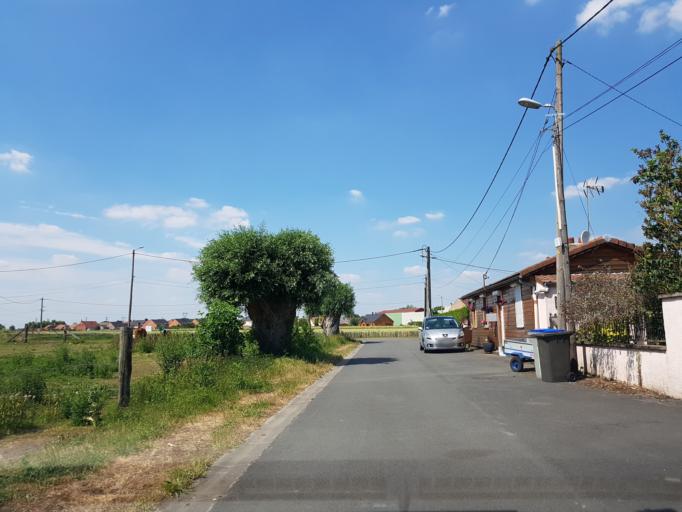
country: FR
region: Nord-Pas-de-Calais
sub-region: Departement du Nord
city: Roeulx
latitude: 50.3014
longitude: 3.3304
